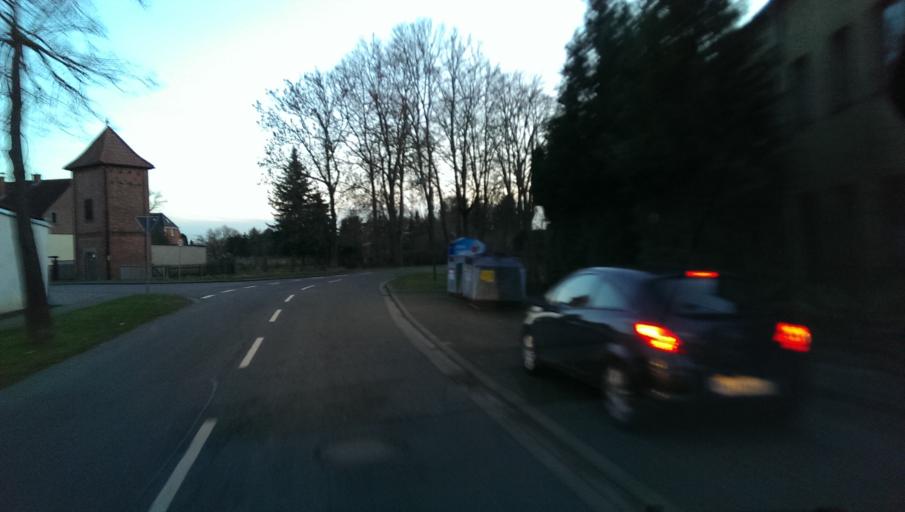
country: DE
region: Saxony-Anhalt
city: Ausleben
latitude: 52.0835
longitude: 11.1219
